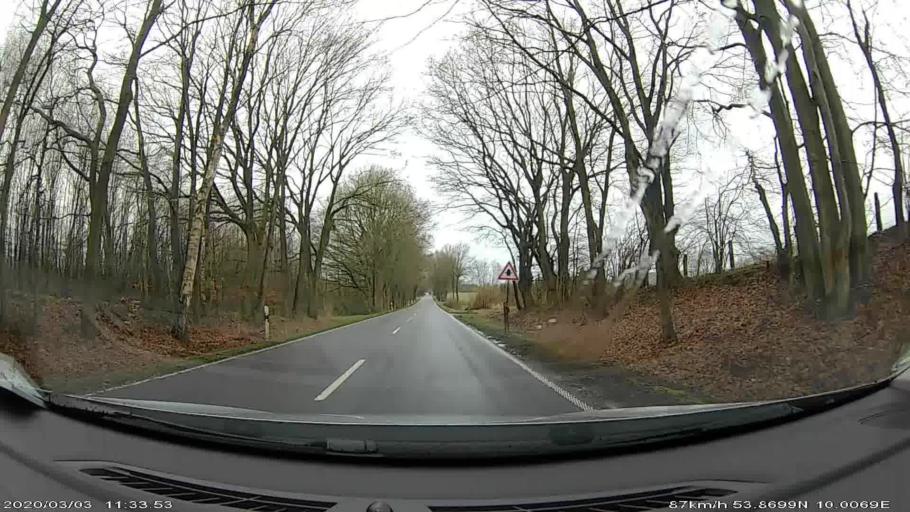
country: DE
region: Schleswig-Holstein
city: Kattendorf
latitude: 53.8716
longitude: 10.0015
